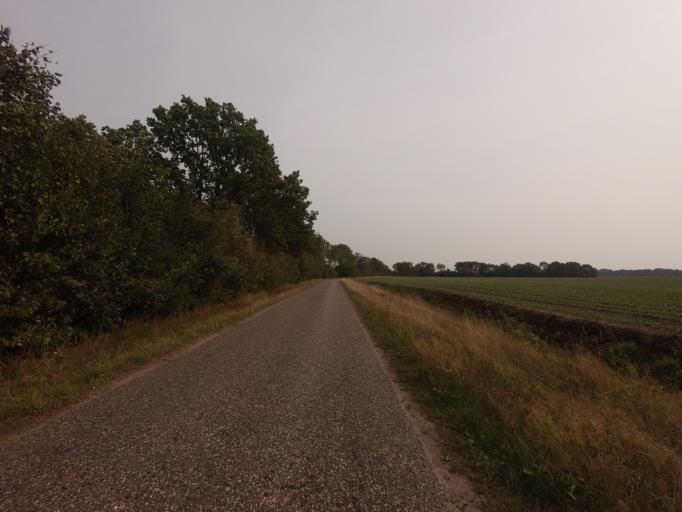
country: NL
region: Drenthe
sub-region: Gemeente Tynaarlo
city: Vries
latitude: 53.1065
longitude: 6.5476
